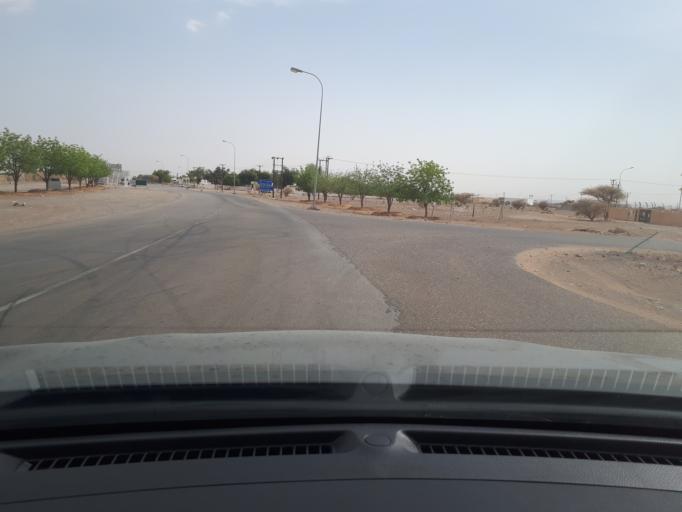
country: OM
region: Ash Sharqiyah
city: Badiyah
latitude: 22.4971
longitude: 58.9384
